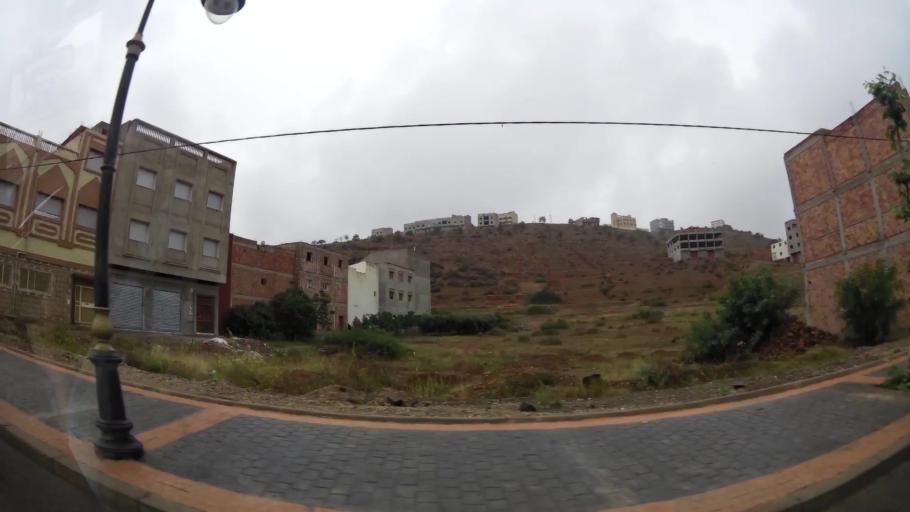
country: MA
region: Taza-Al Hoceima-Taounate
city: Imzourene
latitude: 35.1667
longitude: -3.8575
